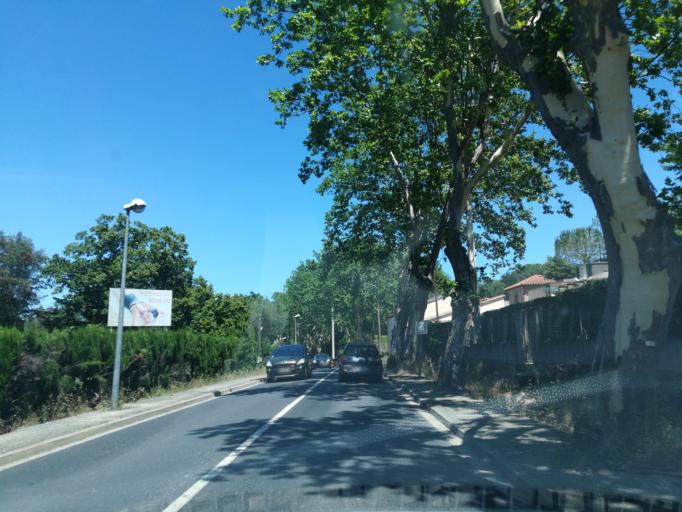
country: FR
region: Languedoc-Roussillon
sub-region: Departement des Pyrenees-Orientales
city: el Volo
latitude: 42.5089
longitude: 2.8262
